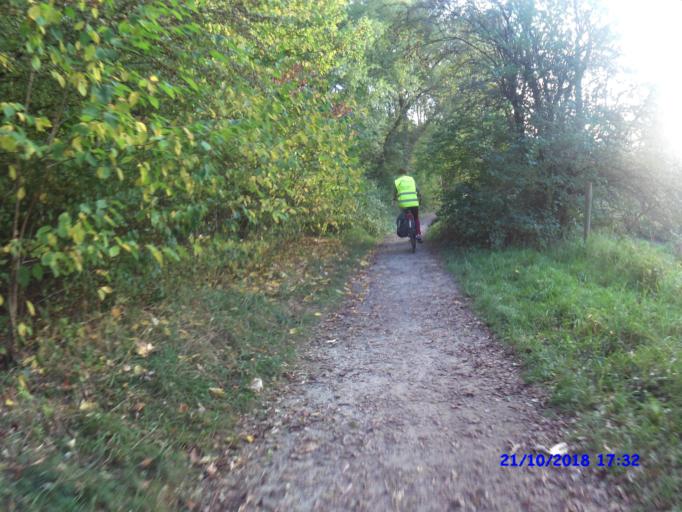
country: BE
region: Flanders
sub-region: Provincie Vlaams-Brabant
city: Kraainem
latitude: 50.8509
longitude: 4.4473
